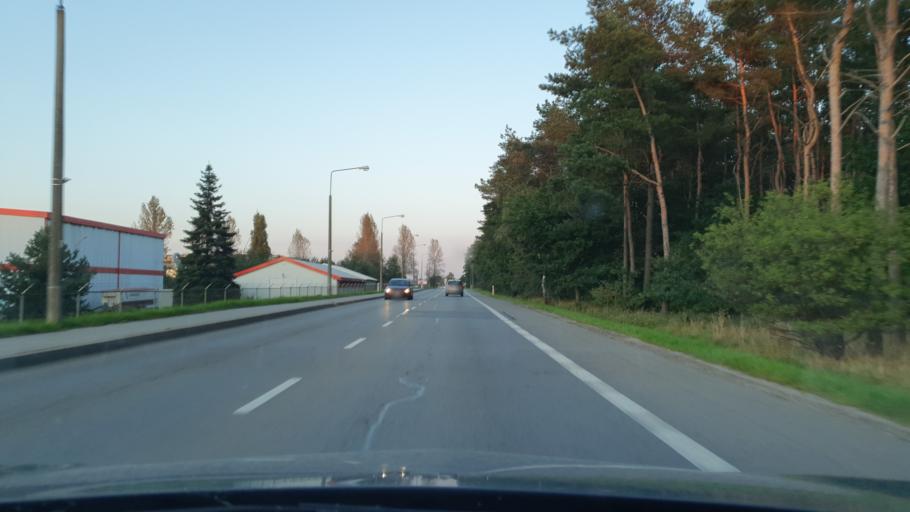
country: PL
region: Pomeranian Voivodeship
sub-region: Powiat leborski
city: Lebork
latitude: 54.5355
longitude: 17.7667
